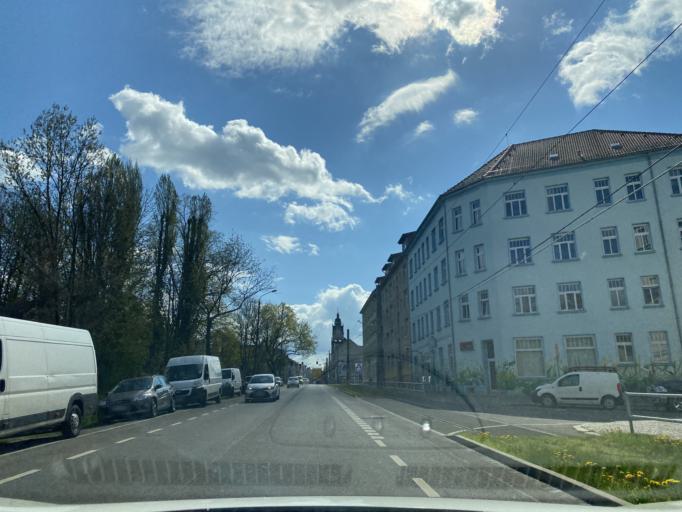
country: DE
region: Saxony
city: Leipzig
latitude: 51.3757
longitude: 12.3181
